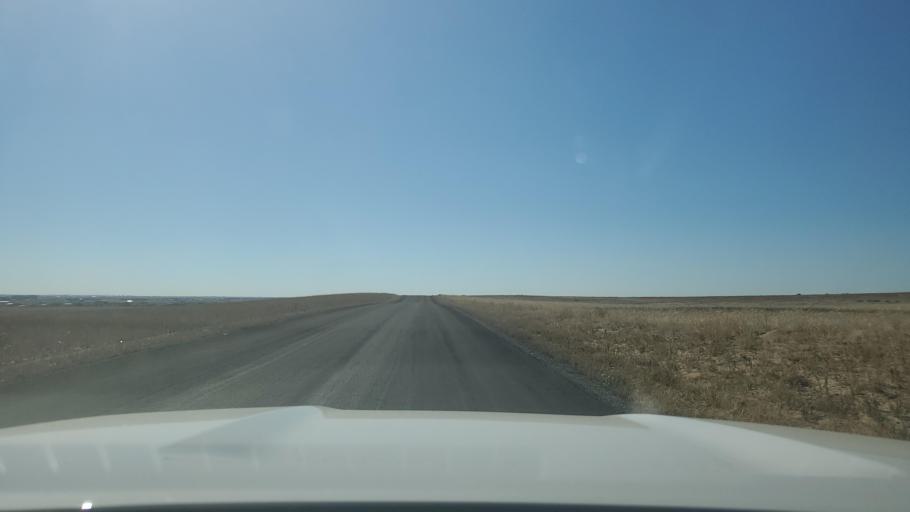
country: US
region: Colorado
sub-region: Adams County
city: Bennett
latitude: 39.7590
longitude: -104.3771
